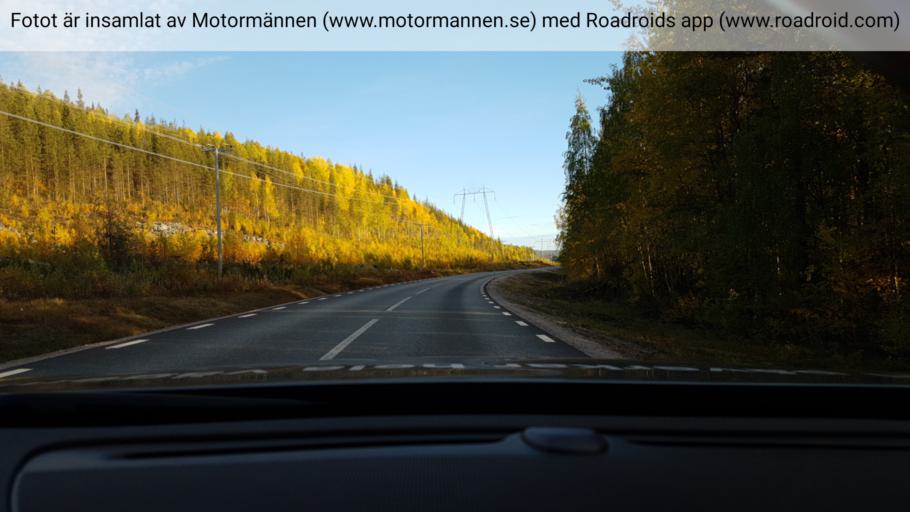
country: SE
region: Norrbotten
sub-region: Jokkmokks Kommun
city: Jokkmokk
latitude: 66.8464
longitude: 19.8350
